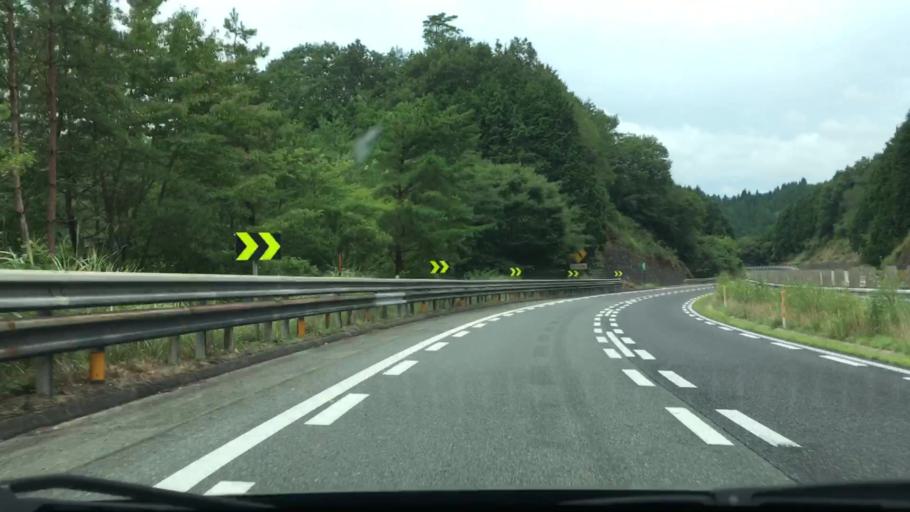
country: JP
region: Hiroshima
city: Shobara
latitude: 34.8848
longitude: 133.1959
